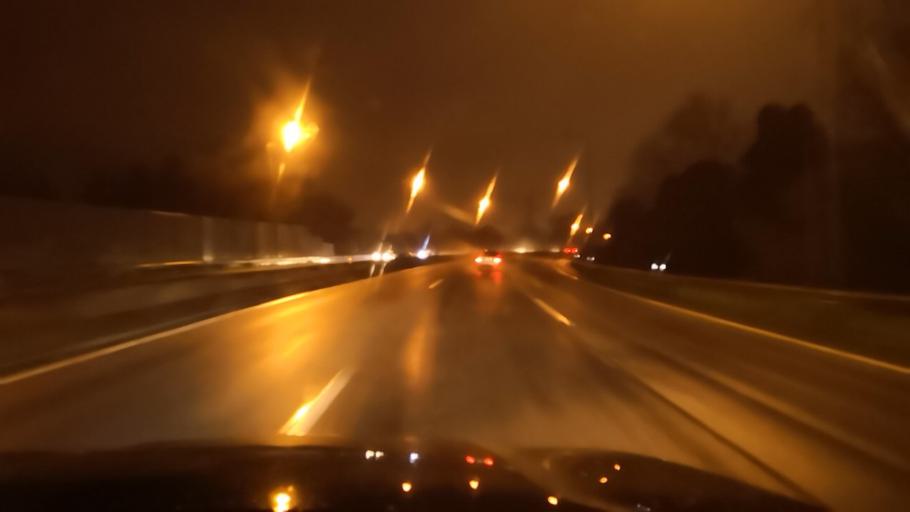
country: PT
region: Porto
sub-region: Vila Nova de Gaia
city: Canidelo
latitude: 41.1210
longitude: -8.6356
